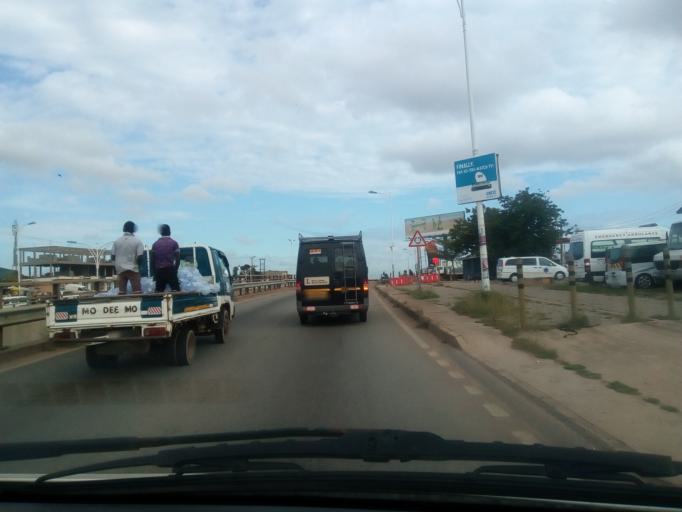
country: GH
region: Greater Accra
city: Dome
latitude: 5.6459
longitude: -0.2476
